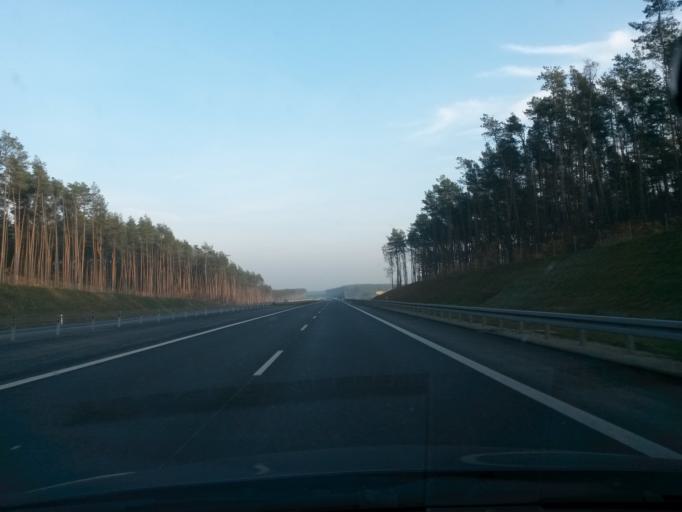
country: PL
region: Greater Poland Voivodeship
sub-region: Powiat kepinski
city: Perzow
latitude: 51.2958
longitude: 17.8288
